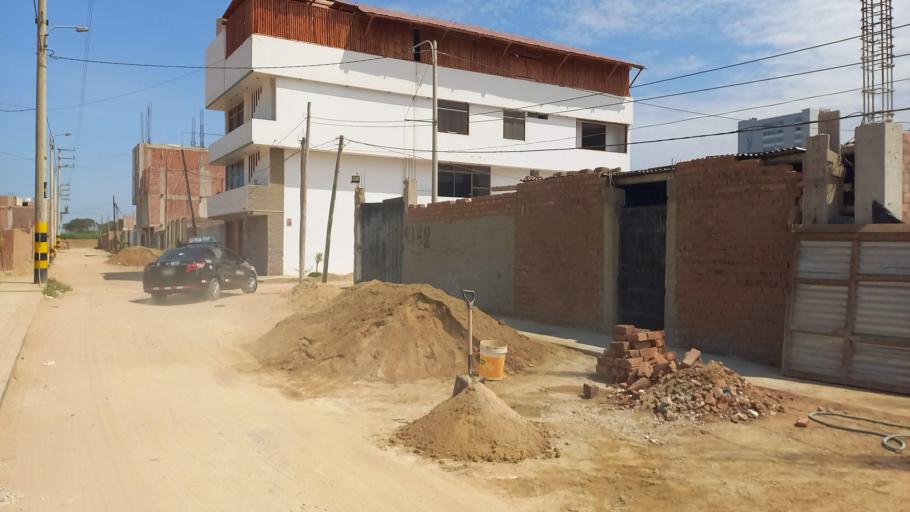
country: PE
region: La Libertad
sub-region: Provincia de Trujillo
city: Trujillo
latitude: -8.1174
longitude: -79.0471
